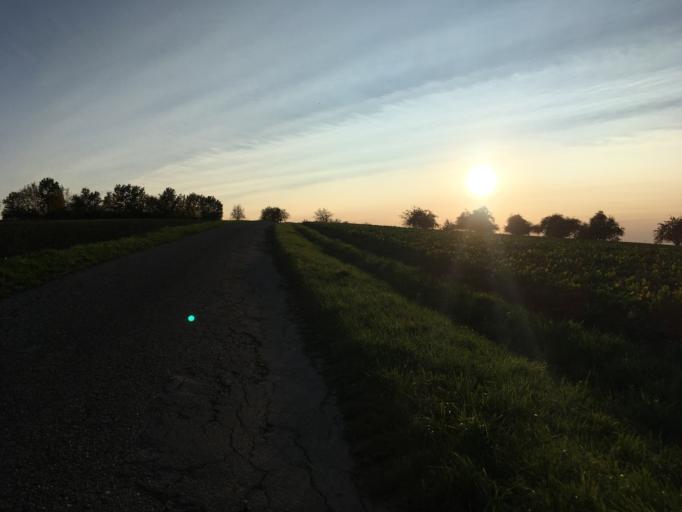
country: DE
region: Baden-Wuerttemberg
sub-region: Regierungsbezirk Stuttgart
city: Neuenstein
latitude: 49.2254
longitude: 9.5525
